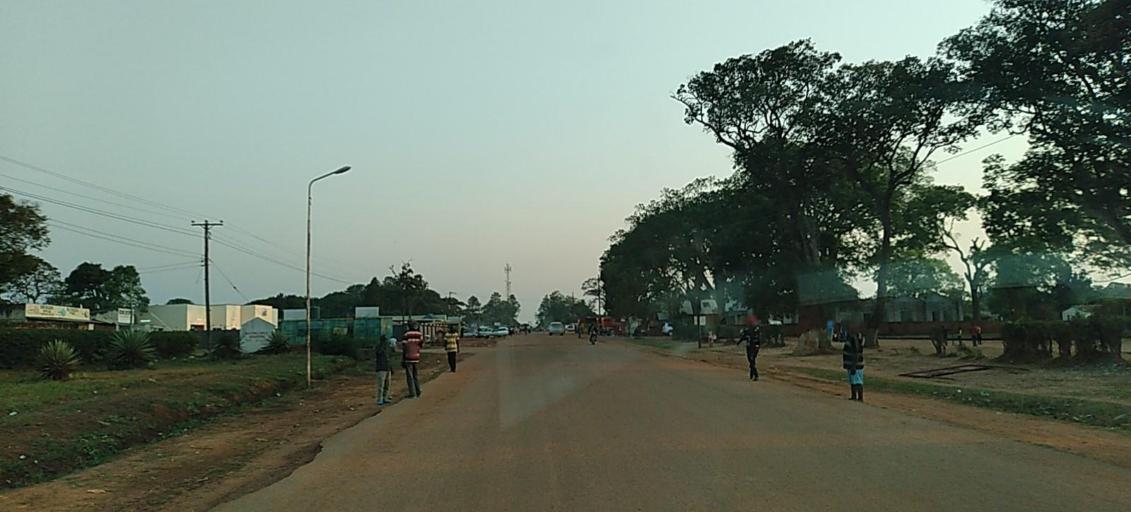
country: ZM
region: North-Western
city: Mwinilunga
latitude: -11.7342
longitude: 24.4311
